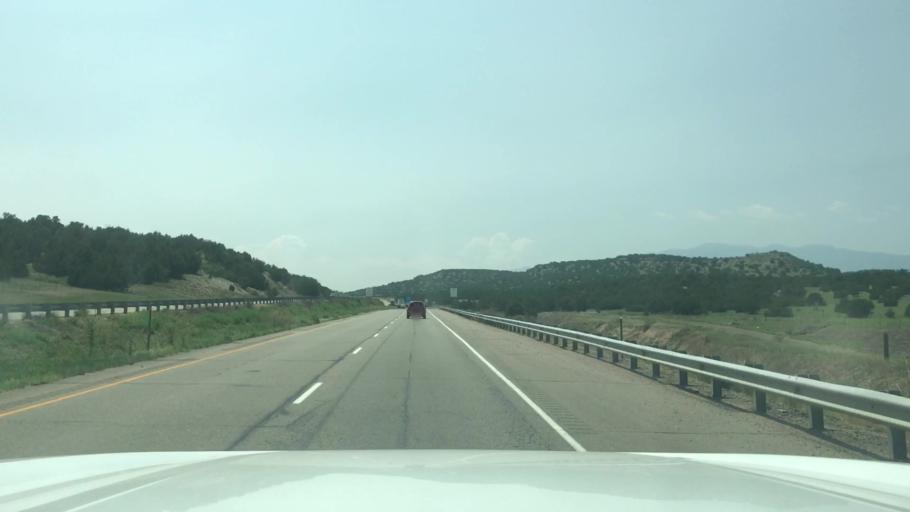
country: US
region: Colorado
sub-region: Pueblo County
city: Colorado City
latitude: 37.9911
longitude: -104.7665
